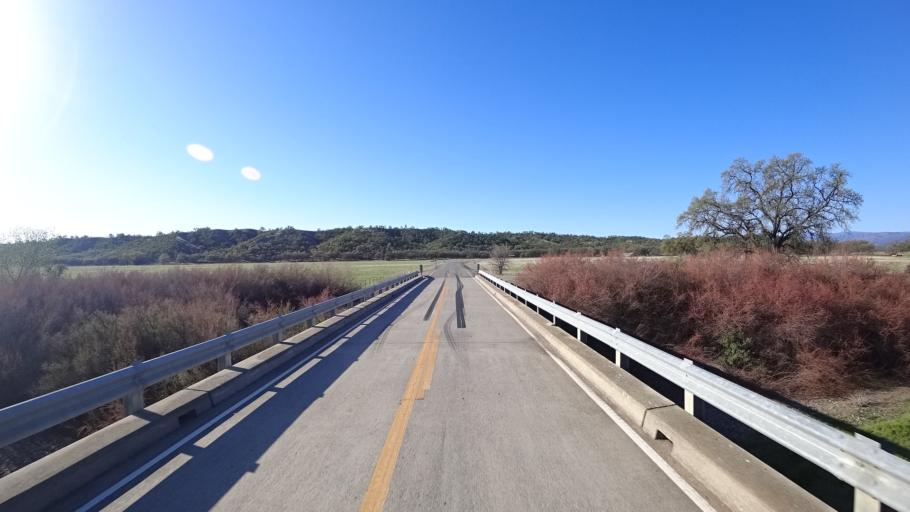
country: US
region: California
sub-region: Tehama County
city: Rancho Tehama Reserve
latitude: 39.8054
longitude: -122.4260
